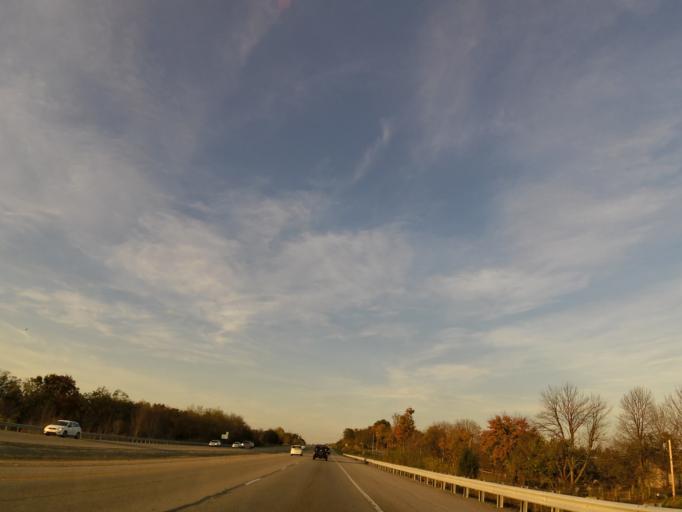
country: US
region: Kentucky
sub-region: Jessamine County
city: Wilmore
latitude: 37.7897
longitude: -84.6055
